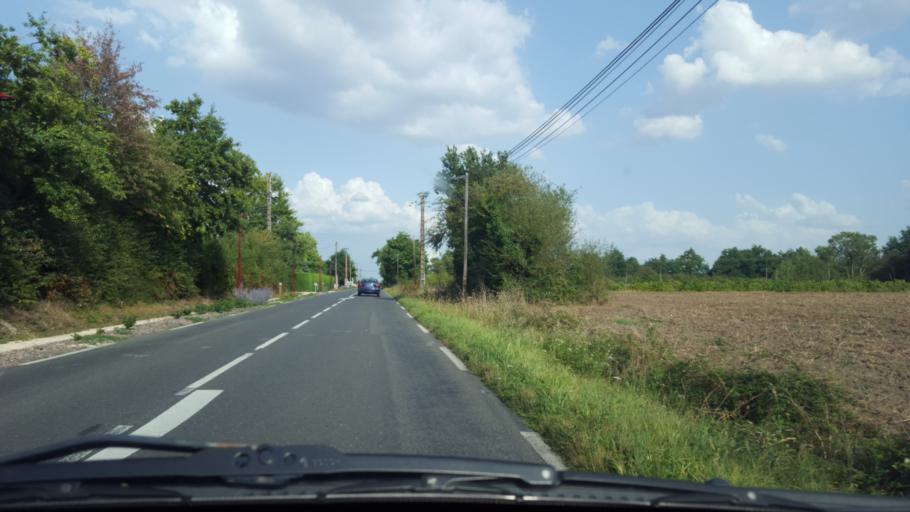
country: FR
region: Pays de la Loire
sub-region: Departement de la Loire-Atlantique
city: Geneston
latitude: 47.0572
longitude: -1.5024
